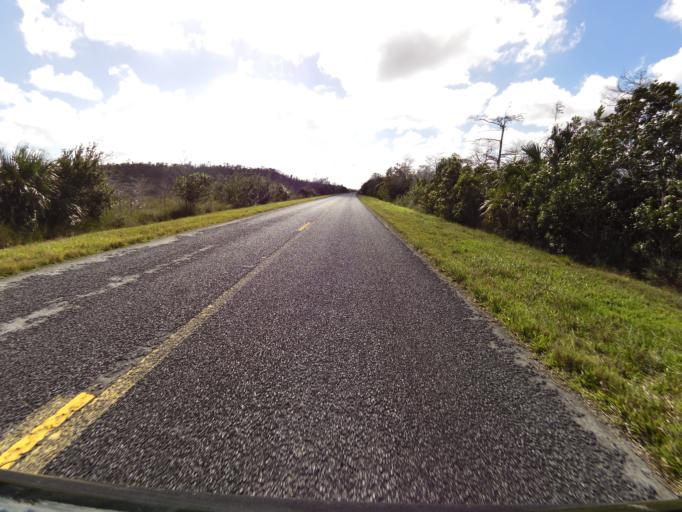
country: US
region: Florida
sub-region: Miami-Dade County
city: Florida City
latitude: 25.4145
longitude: -80.7815
